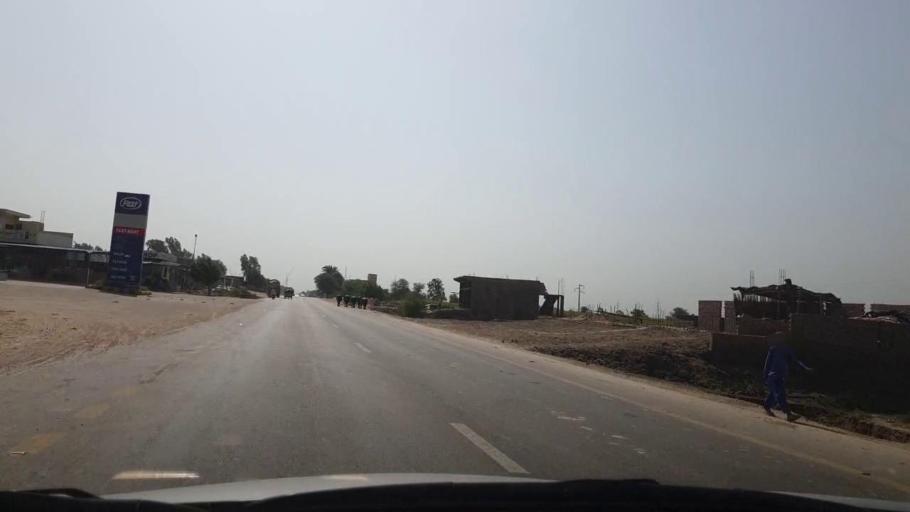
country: PK
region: Sindh
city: Tando Muhammad Khan
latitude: 25.1036
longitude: 68.5873
